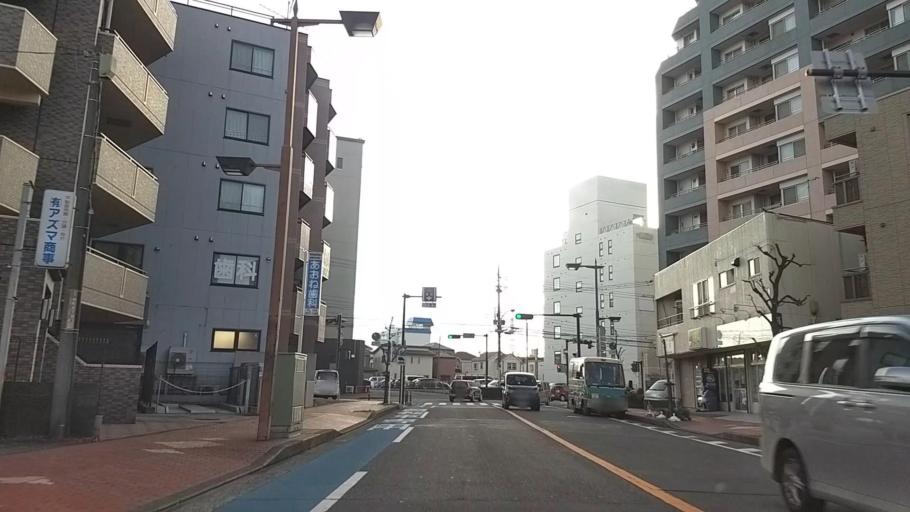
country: JP
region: Kanagawa
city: Atsugi
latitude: 35.4356
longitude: 139.3623
